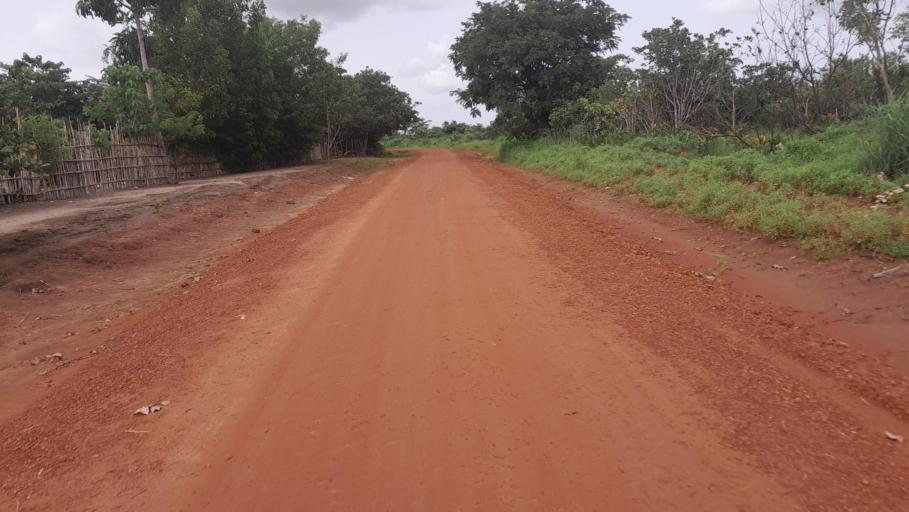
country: GN
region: Boke
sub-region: Boffa
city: Boffa
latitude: 10.0665
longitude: -13.8676
